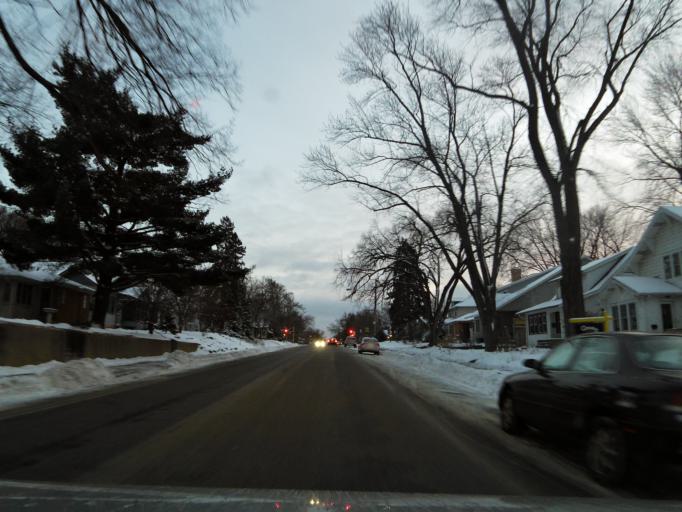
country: US
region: Minnesota
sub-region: Hennepin County
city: Edina
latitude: 44.9154
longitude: -93.3189
